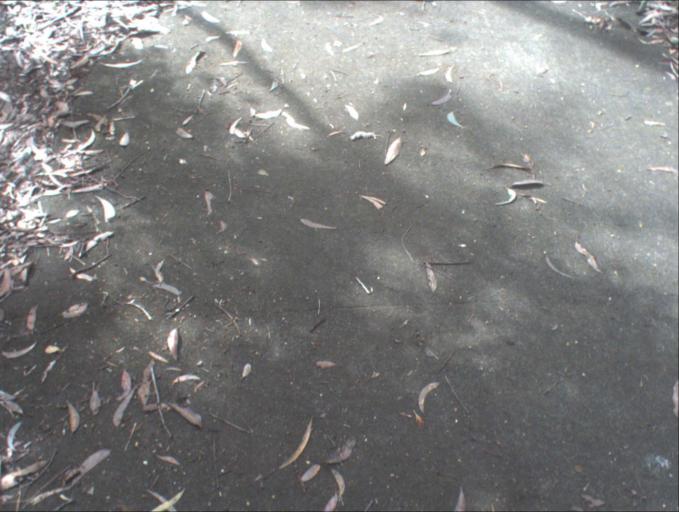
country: AU
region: Queensland
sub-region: Logan
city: Logan Reserve
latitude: -27.6786
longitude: 153.0622
